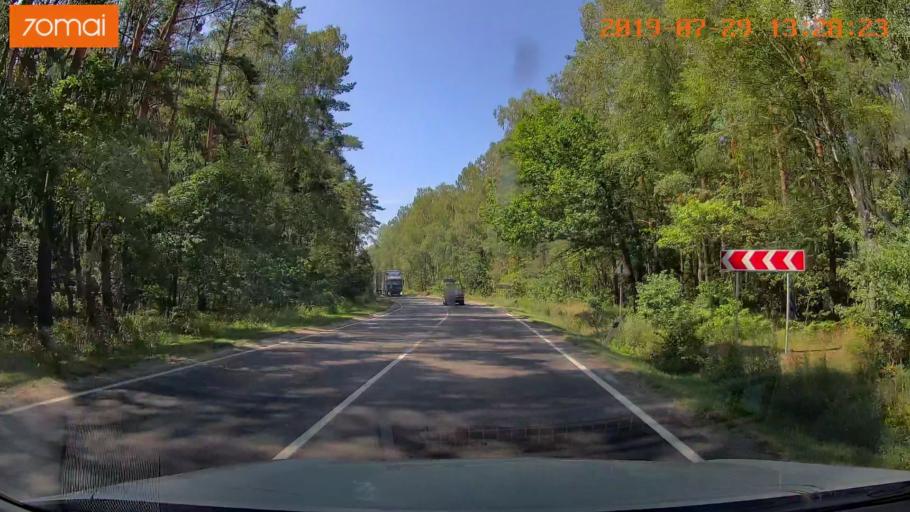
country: RU
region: Kaliningrad
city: Vzmorye
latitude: 54.7048
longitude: 20.2829
